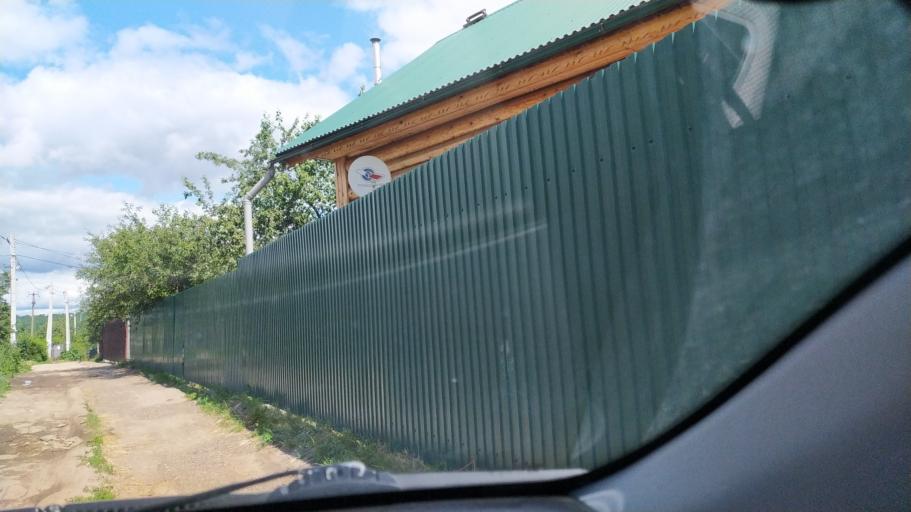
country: RU
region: Chuvashia
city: Novyye Lapsary
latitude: 56.1130
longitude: 47.1752
